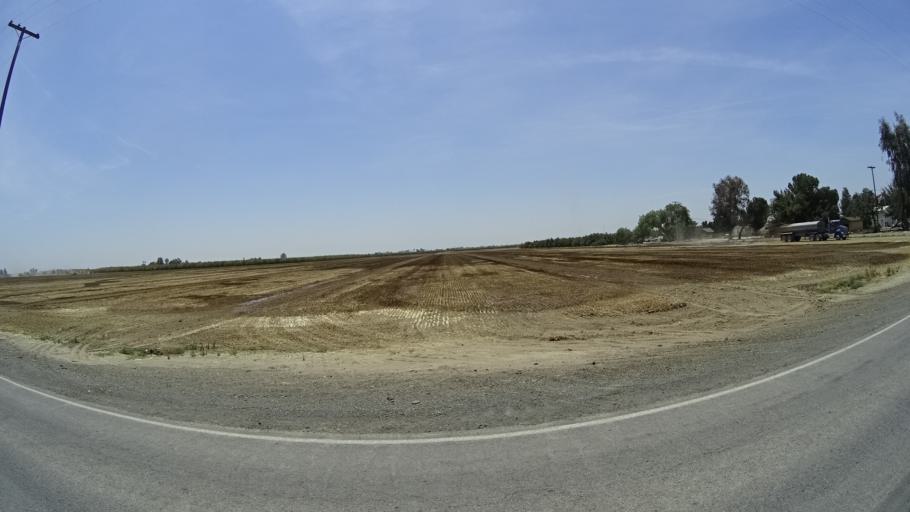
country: US
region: California
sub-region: Fresno County
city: Riverdale
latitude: 36.4021
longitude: -119.8468
